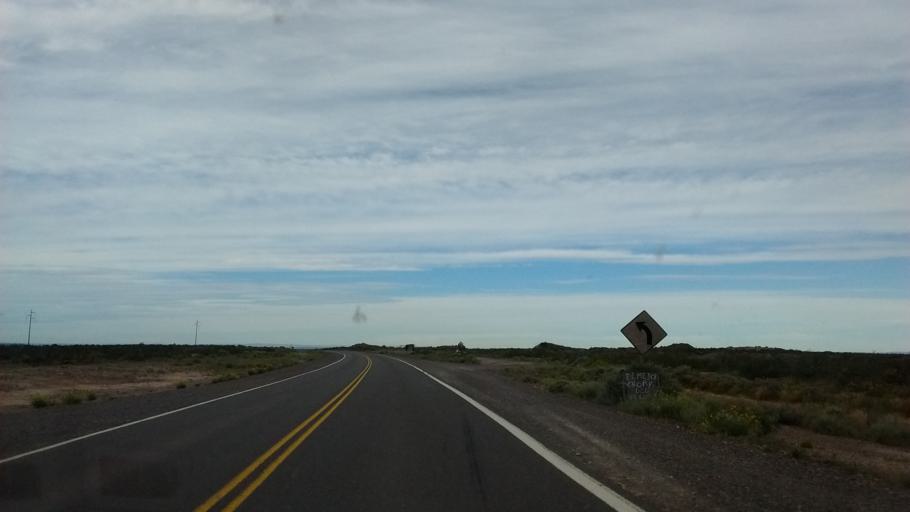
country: AR
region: Rio Negro
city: Contraalmirante Cordero
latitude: -38.5900
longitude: -68.1049
